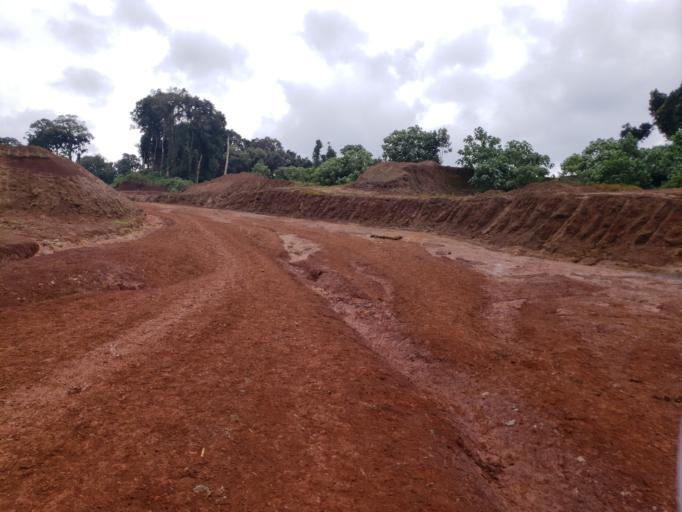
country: ET
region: Oromiya
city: Dodola
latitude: 6.5788
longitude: 39.4188
